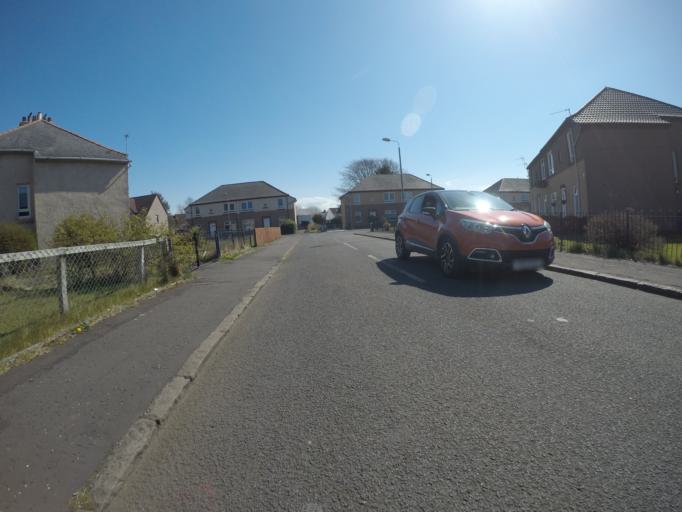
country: GB
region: Scotland
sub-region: North Ayrshire
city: Irvine
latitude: 55.6187
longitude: -4.6527
